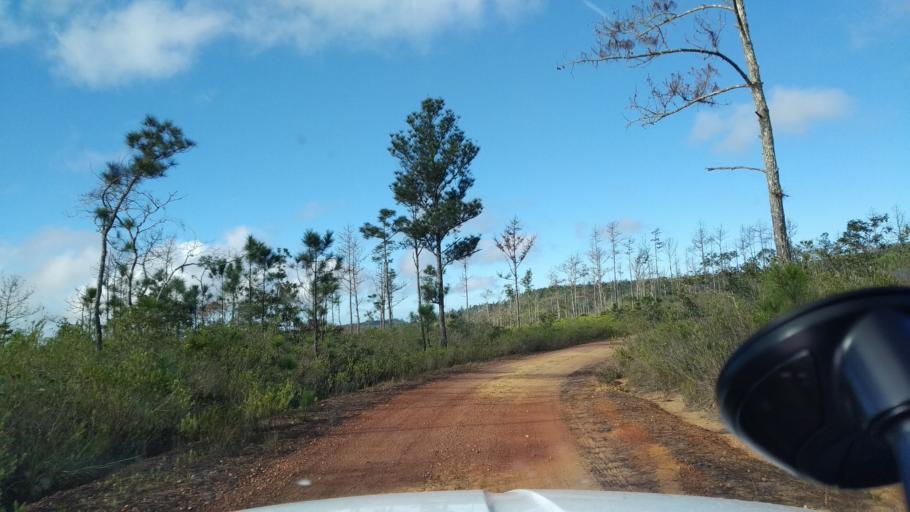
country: BZ
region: Cayo
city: Belmopan
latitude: 16.9954
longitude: -88.8357
